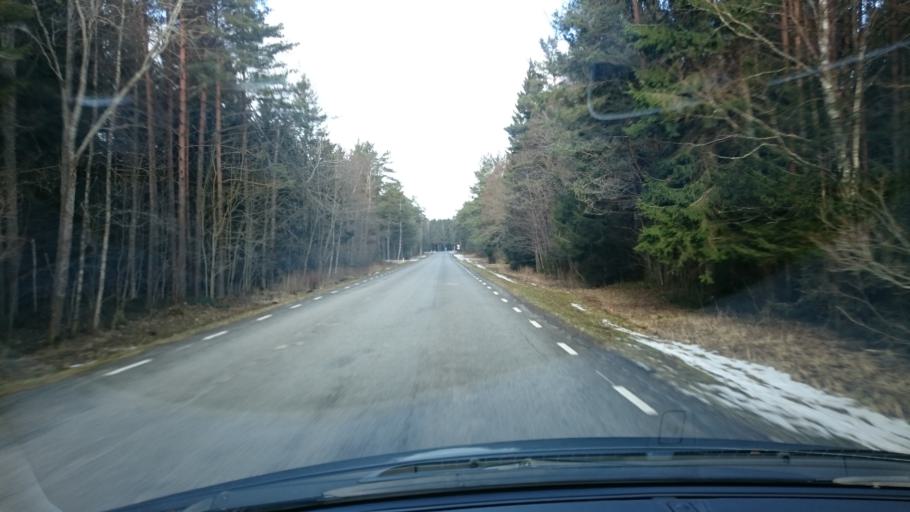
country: EE
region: Harju
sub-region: Keila linn
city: Keila
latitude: 59.3893
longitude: 24.2958
